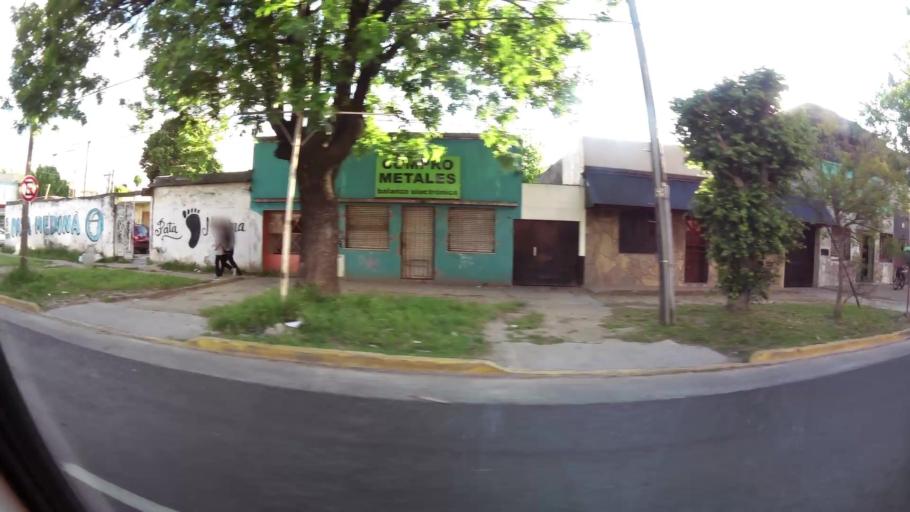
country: AR
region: Buenos Aires
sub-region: Partido de La Plata
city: La Plata
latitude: -34.8950
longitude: -57.9435
